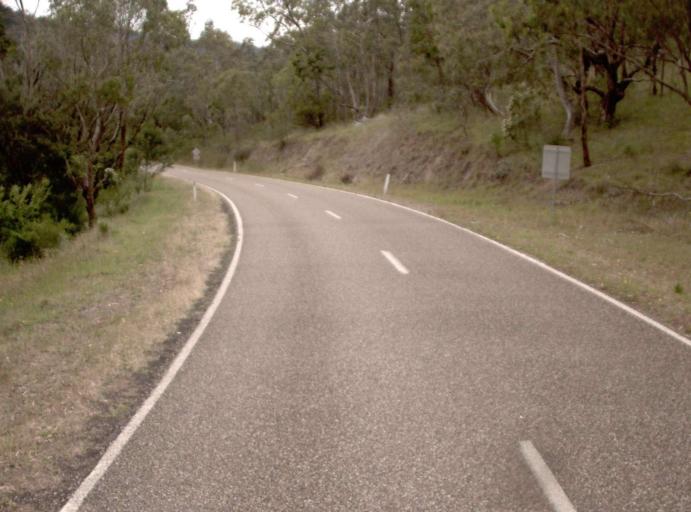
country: AU
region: Victoria
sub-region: East Gippsland
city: Bairnsdale
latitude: -37.5372
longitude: 147.2110
